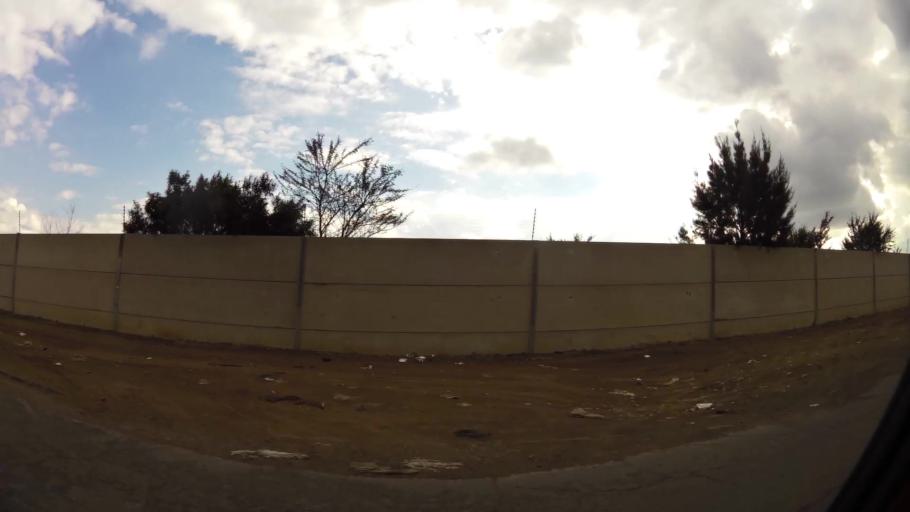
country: ZA
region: Gauteng
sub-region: Sedibeng District Municipality
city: Vanderbijlpark
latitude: -26.6753
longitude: 27.8181
